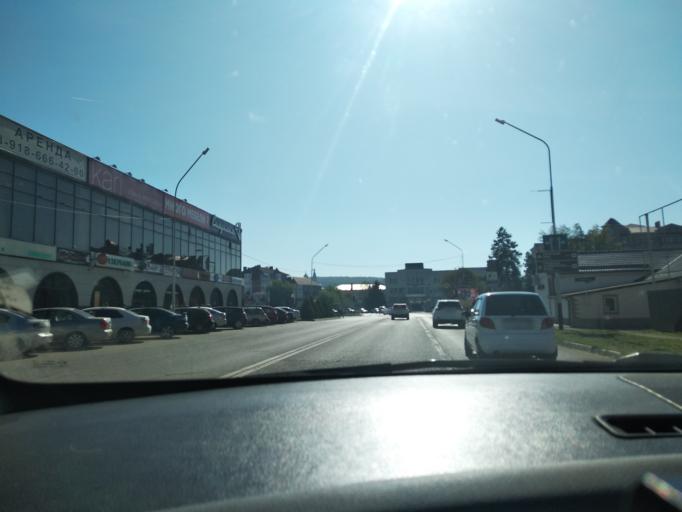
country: RU
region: Krasnodarskiy
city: Goryachiy Klyuch
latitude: 44.6352
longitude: 39.1351
